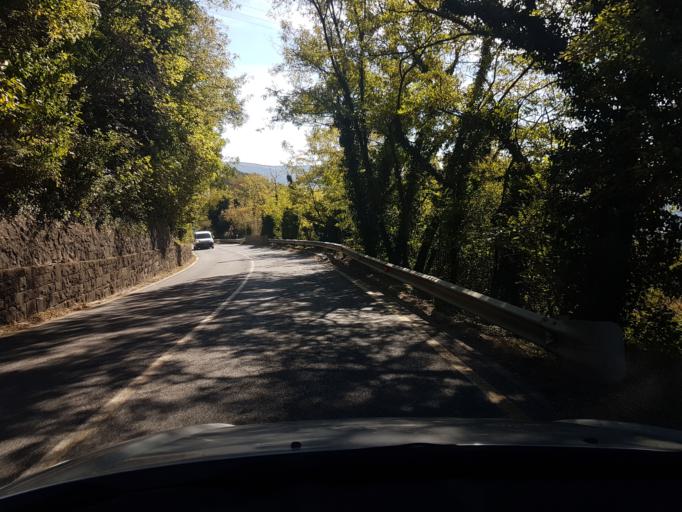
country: IT
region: Friuli Venezia Giulia
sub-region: Provincia di Trieste
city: Domio
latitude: 45.6316
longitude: 13.8414
